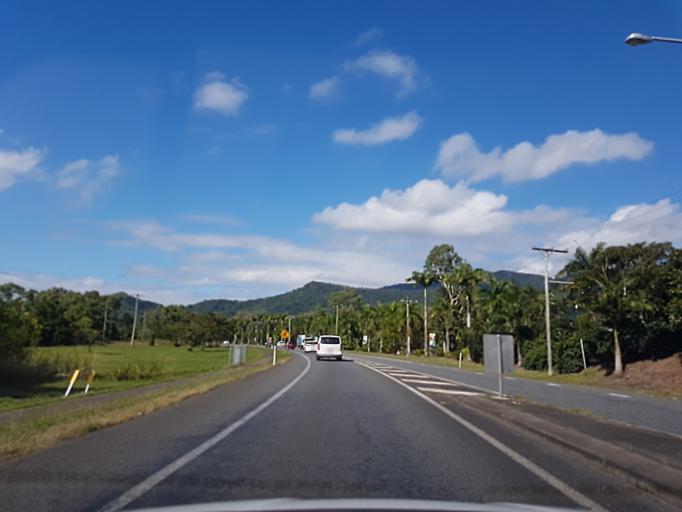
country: AU
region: Queensland
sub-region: Cairns
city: Trinity Beach
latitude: -16.7835
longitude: 145.6734
